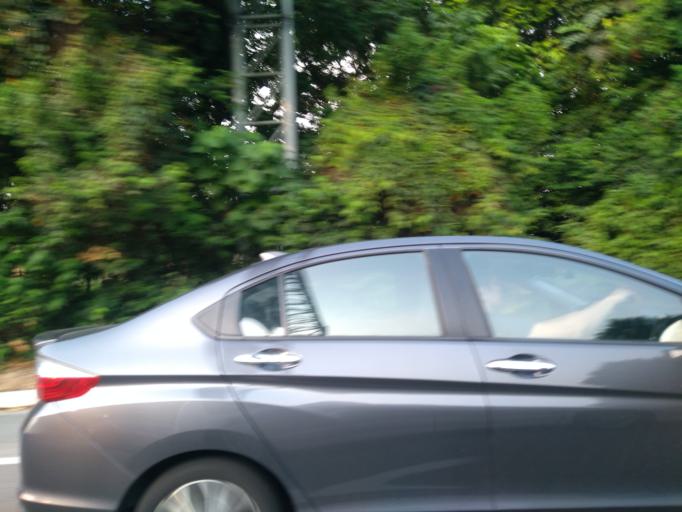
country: MY
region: Kuala Lumpur
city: Kuala Lumpur
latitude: 3.1248
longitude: 101.7031
